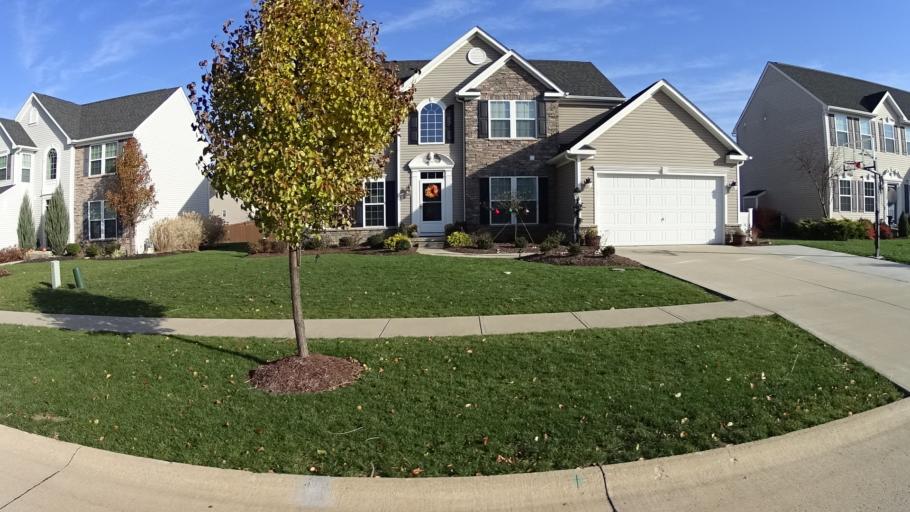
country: US
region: Ohio
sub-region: Lorain County
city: Avon
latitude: 41.4545
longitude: -82.0568
